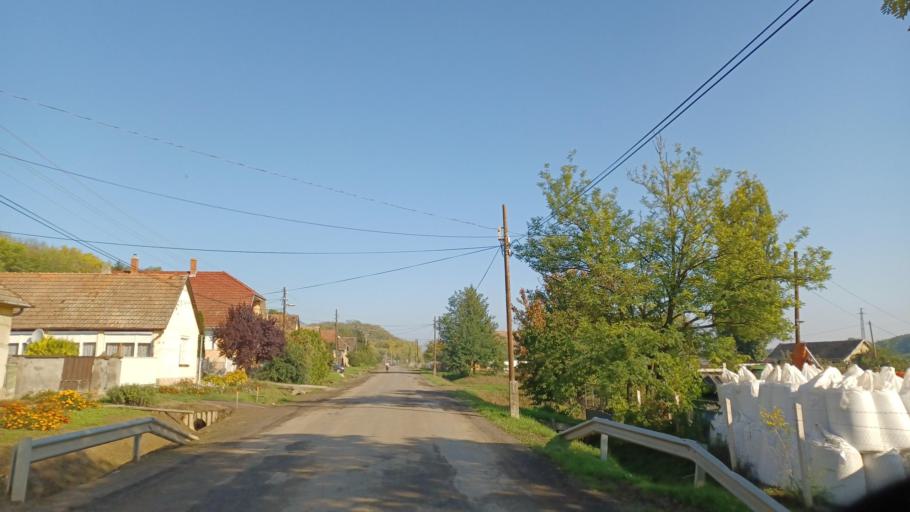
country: HU
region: Tolna
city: Szedres
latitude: 46.5151
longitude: 18.5906
